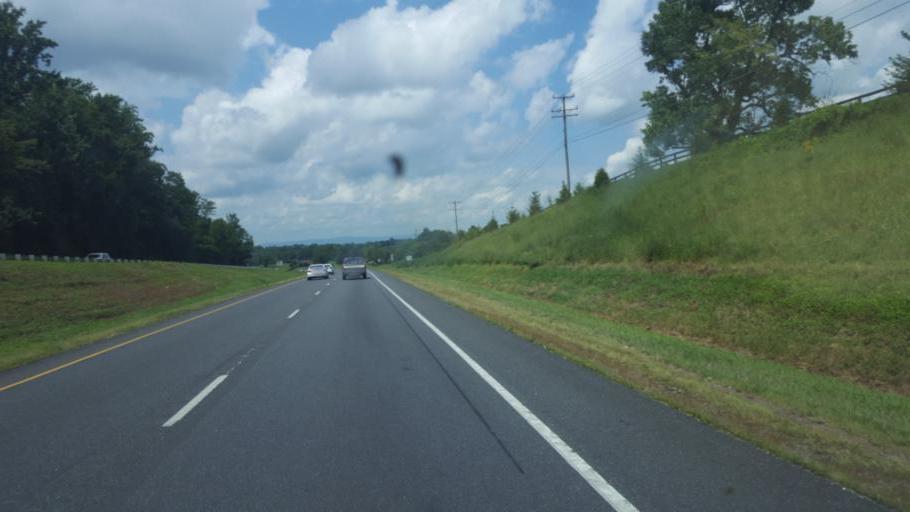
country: US
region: Virginia
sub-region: Fauquier County
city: Marshall
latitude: 38.8194
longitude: -77.8140
